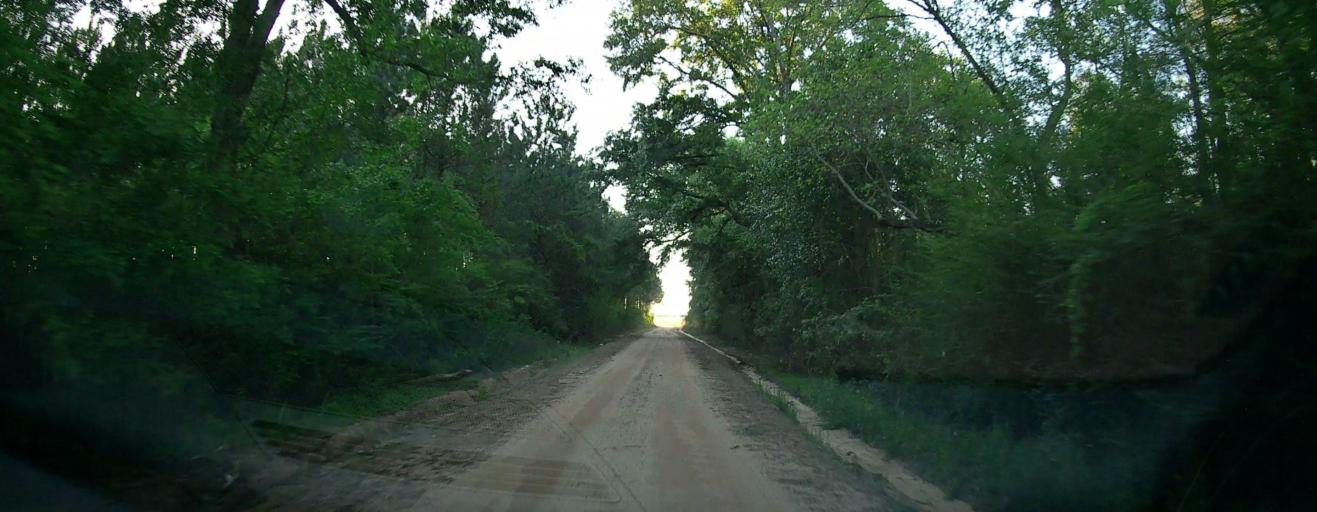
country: US
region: Georgia
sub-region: Irwin County
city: Ocilla
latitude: 31.6511
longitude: -83.2304
